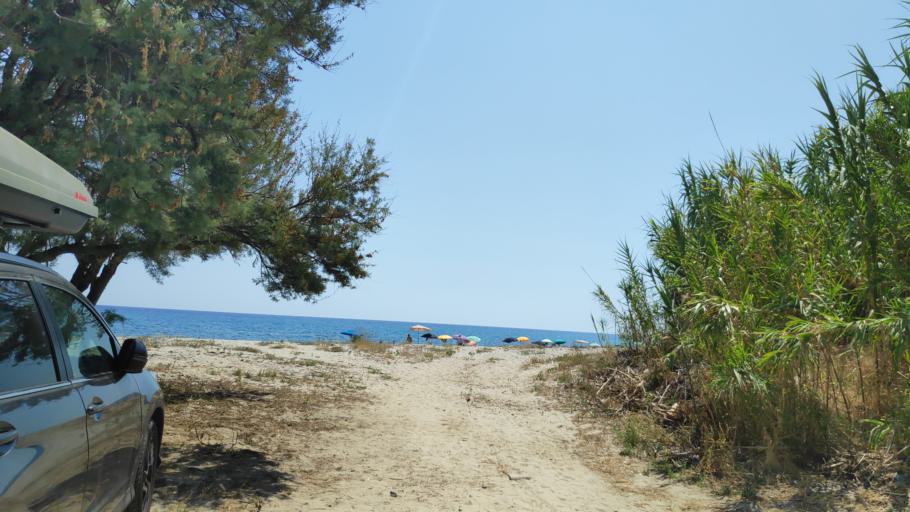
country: IT
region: Calabria
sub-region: Provincia di Catanzaro
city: Guardavalle Marina
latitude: 38.5039
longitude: 16.5781
